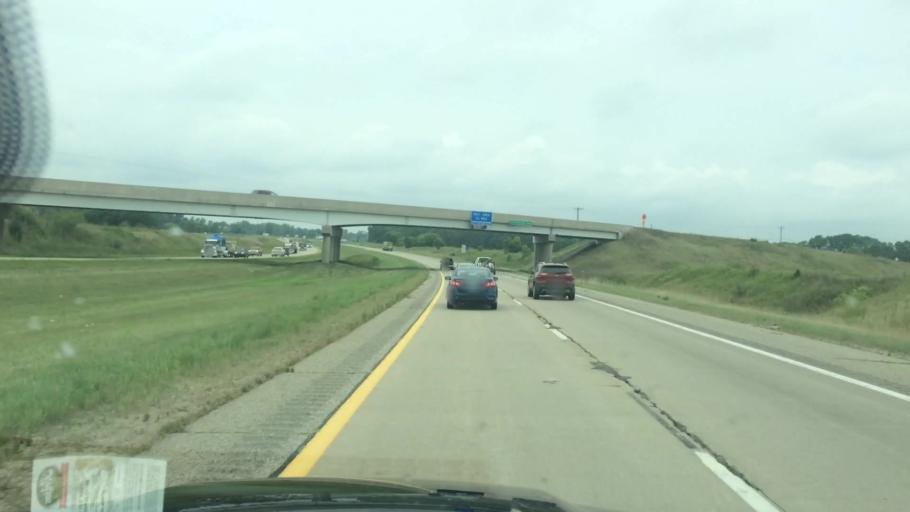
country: US
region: Michigan
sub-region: Eaton County
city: Potterville
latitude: 42.6249
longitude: -84.7306
